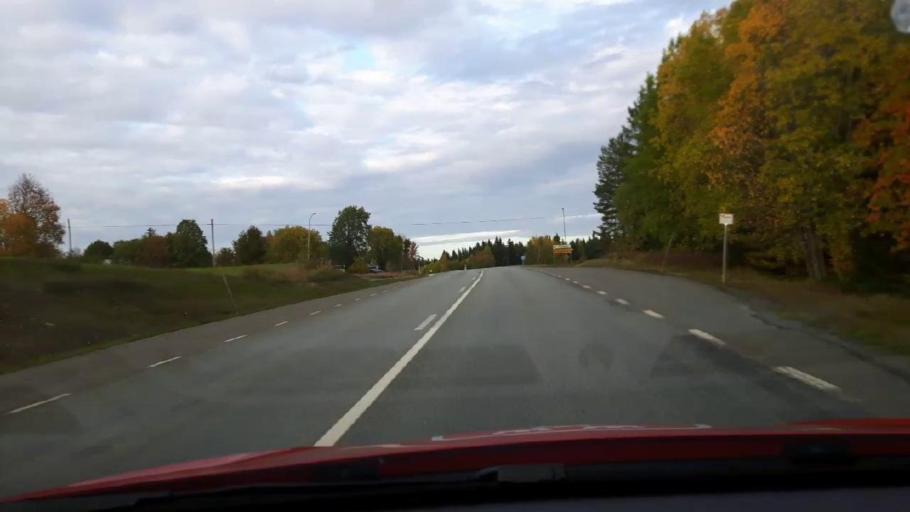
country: SE
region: Jaemtland
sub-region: Krokoms Kommun
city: Krokom
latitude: 63.3617
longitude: 14.5020
